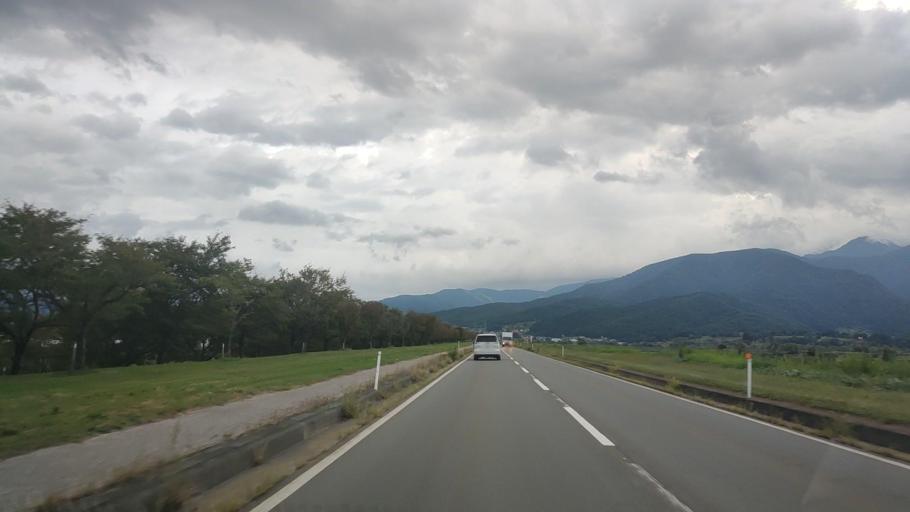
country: JP
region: Nagano
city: Iiyama
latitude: 36.8770
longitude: 138.3828
